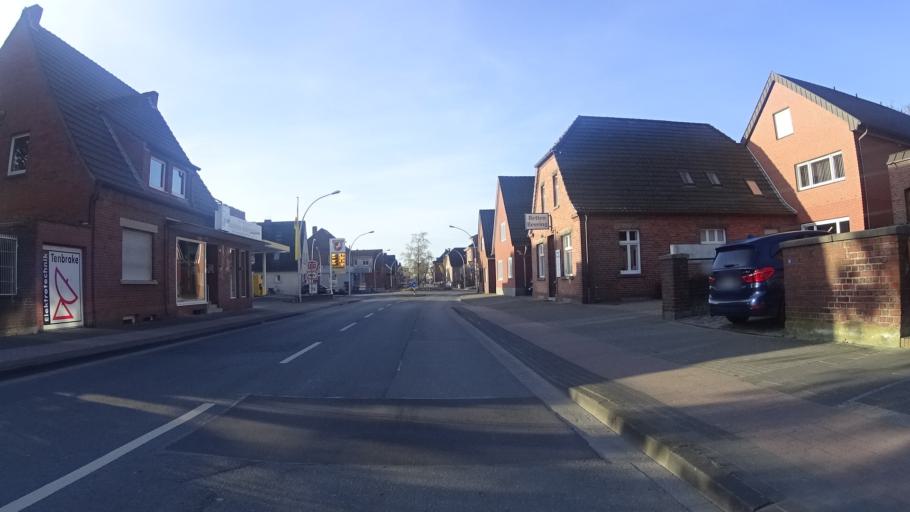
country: DE
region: North Rhine-Westphalia
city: Emsdetten
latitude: 52.1825
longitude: 7.5205
